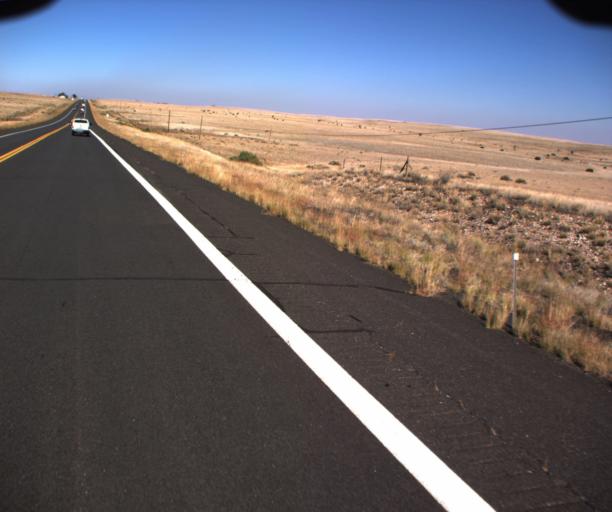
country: US
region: Arizona
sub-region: Coconino County
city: Flagstaff
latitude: 35.5802
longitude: -111.5298
